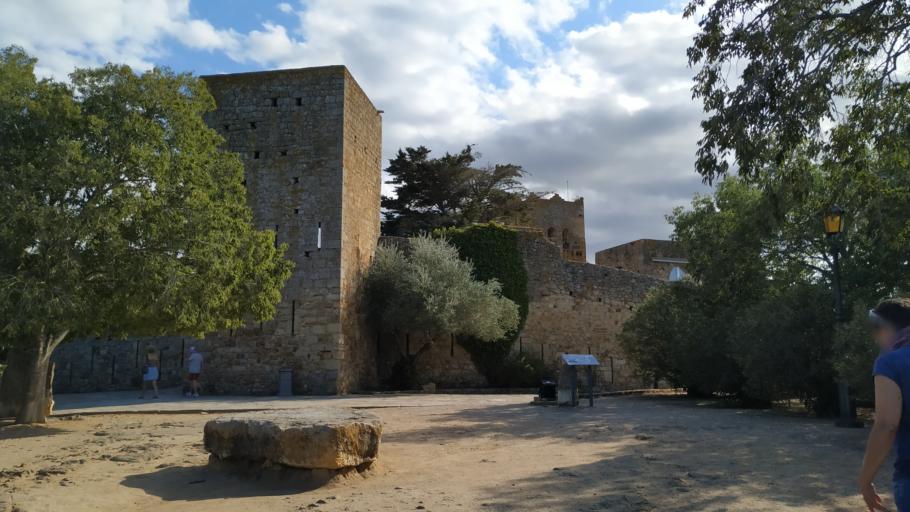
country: ES
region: Catalonia
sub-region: Provincia de Girona
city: Pals
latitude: 41.9725
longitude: 3.1438
